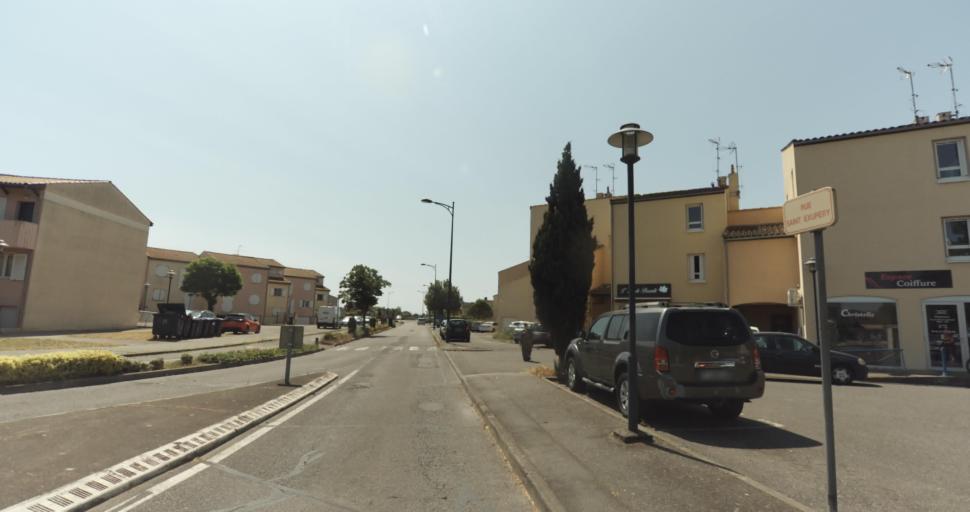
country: FR
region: Midi-Pyrenees
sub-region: Departement de la Haute-Garonne
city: Plaisance-du-Touch
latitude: 43.5622
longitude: 1.3043
